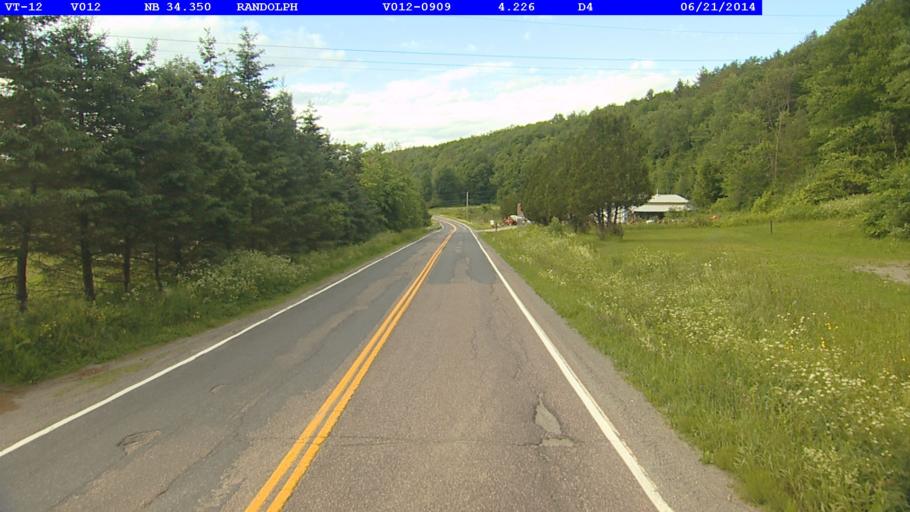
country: US
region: Vermont
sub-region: Orange County
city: Randolph
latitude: 43.9493
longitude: -72.6521
